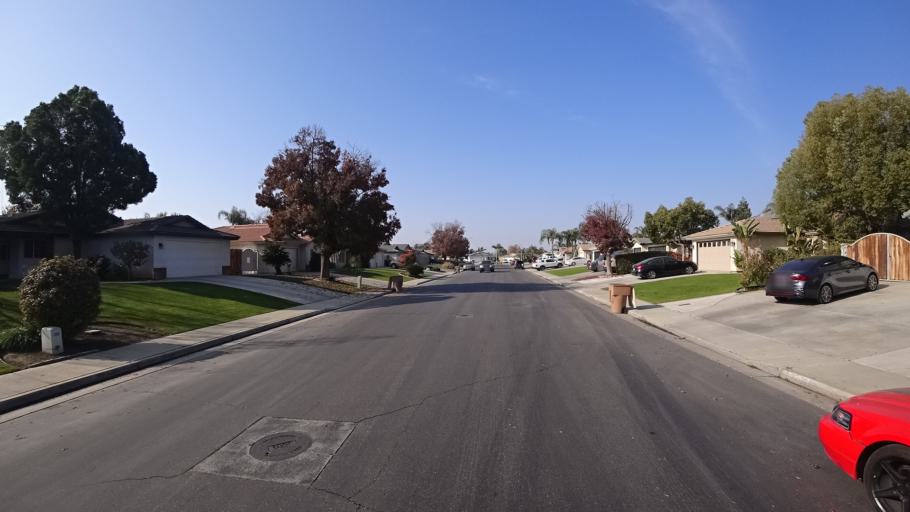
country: US
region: California
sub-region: Kern County
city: Greenacres
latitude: 35.4069
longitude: -119.1164
